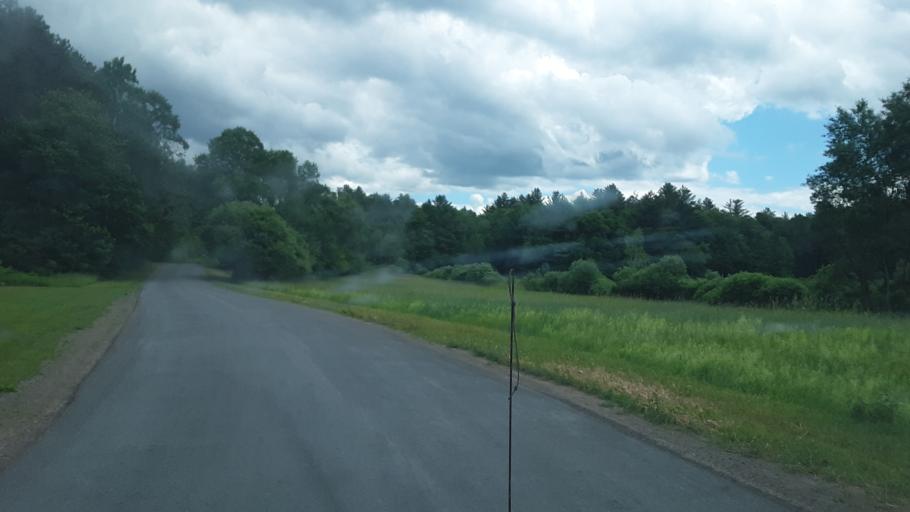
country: US
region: New York
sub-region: Oneida County
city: Rome
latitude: 43.3996
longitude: -75.5347
